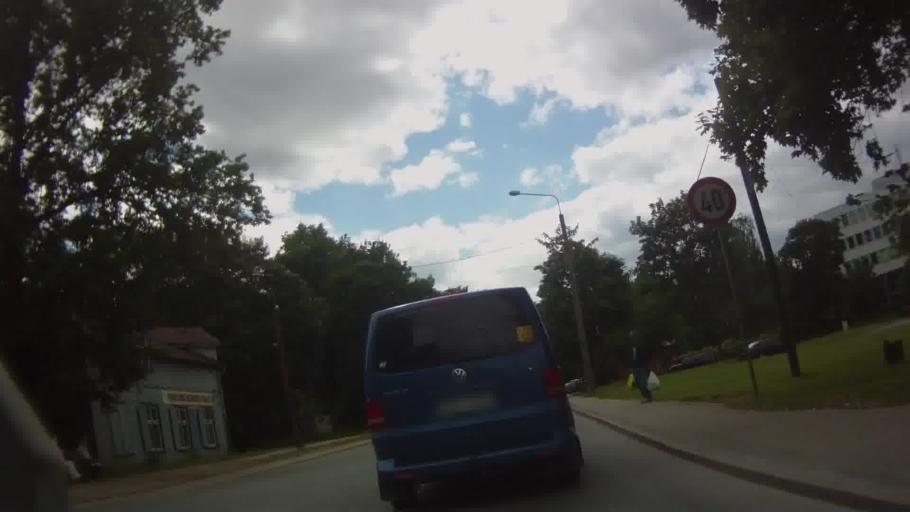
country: LV
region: Riga
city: Riga
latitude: 56.9142
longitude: 24.1215
